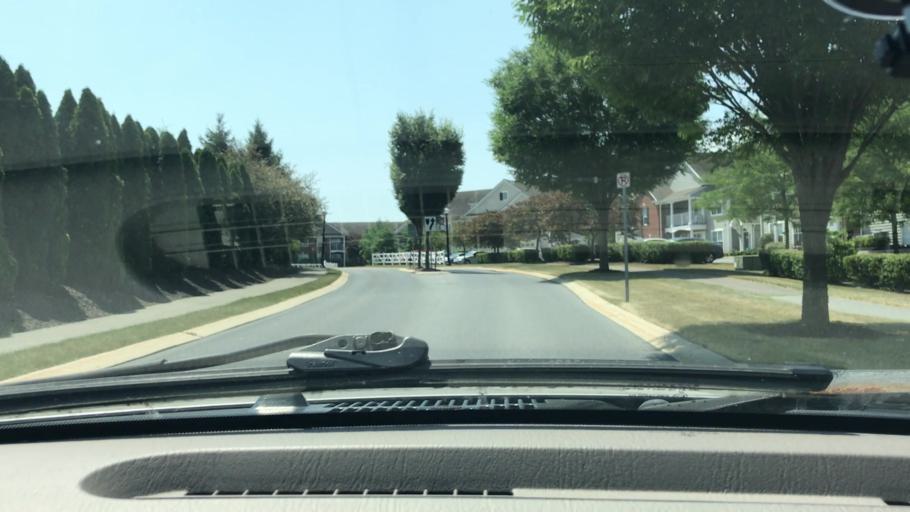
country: US
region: Pennsylvania
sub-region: Lancaster County
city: Mount Joy
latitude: 40.1188
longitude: -76.4814
